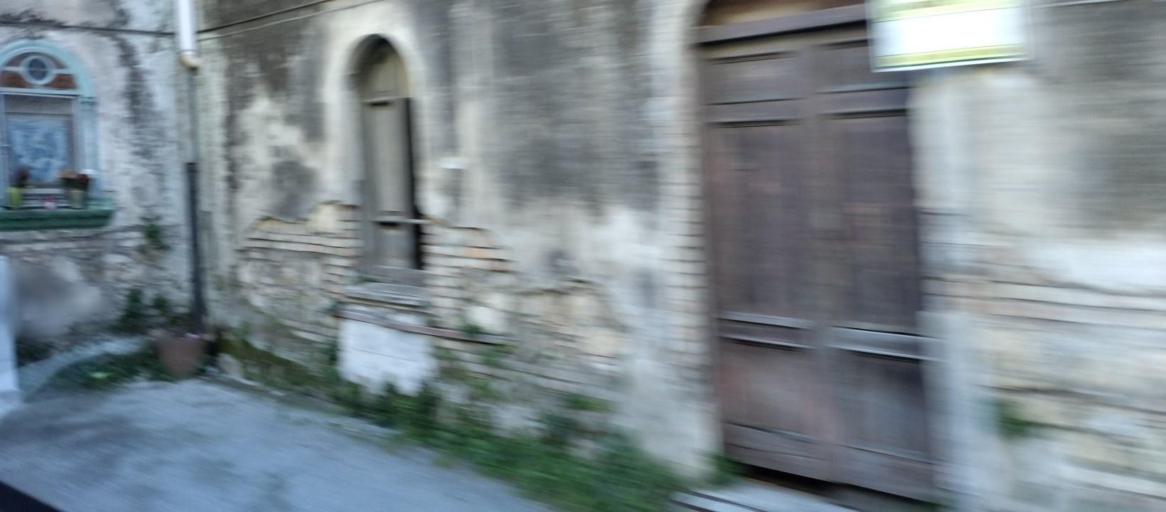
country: IT
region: Calabria
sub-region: Provincia di Catanzaro
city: Catanzaro
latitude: 38.8939
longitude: 16.6016
